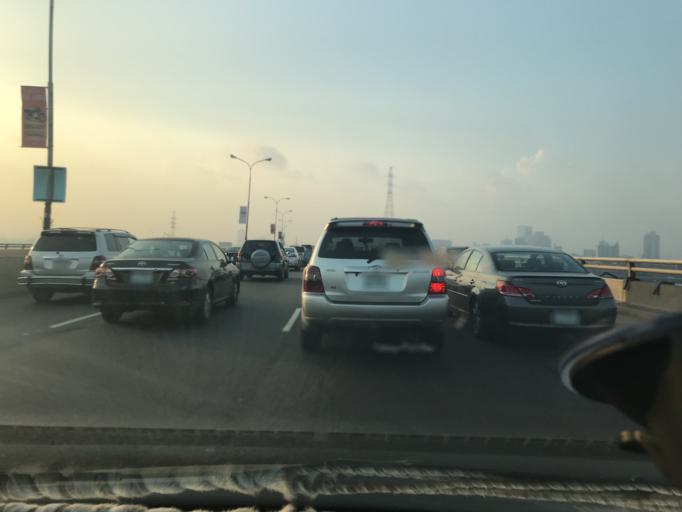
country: NG
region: Lagos
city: Ebute Metta
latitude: 6.4706
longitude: 3.3904
